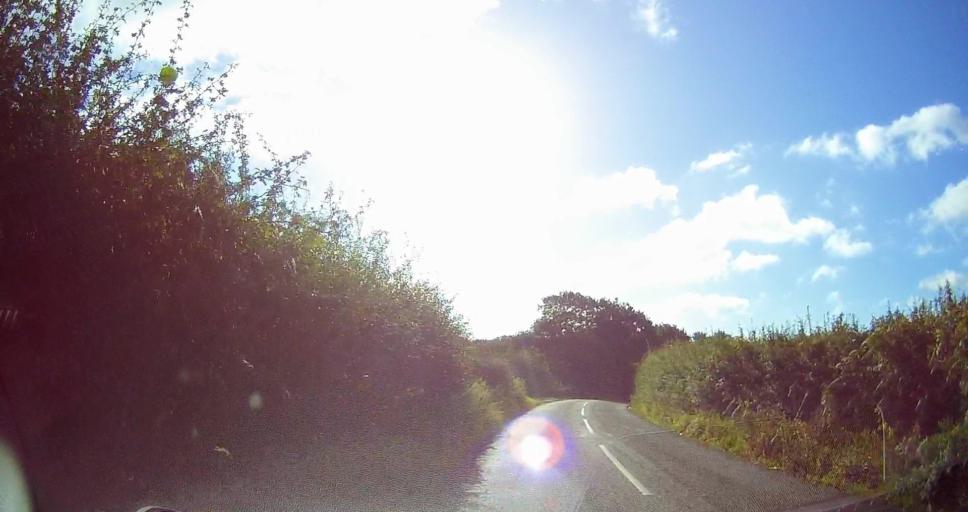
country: GB
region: England
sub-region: Kent
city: Borough Green
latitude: 51.3168
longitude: 0.2797
